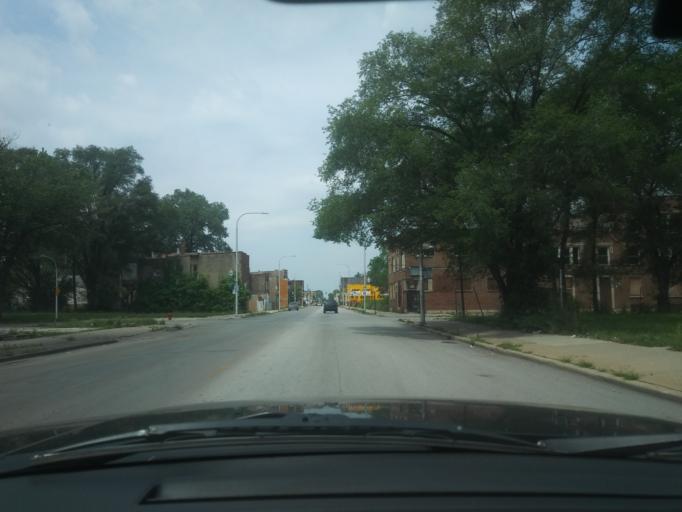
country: US
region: Illinois
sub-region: Cook County
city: Chicago
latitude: 41.7870
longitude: -87.6469
